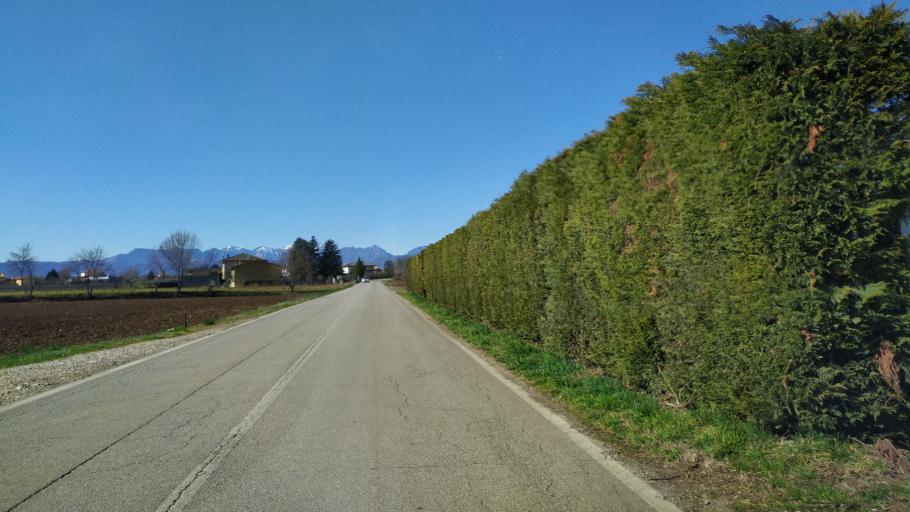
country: IT
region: Veneto
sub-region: Provincia di Vicenza
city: Sandrigo
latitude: 45.6882
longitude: 11.5902
